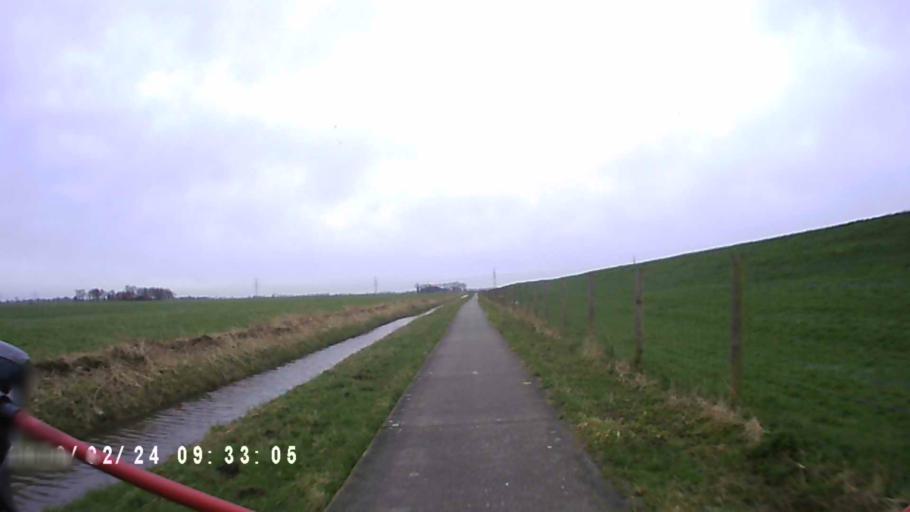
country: NL
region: Groningen
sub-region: Gemeente Winsum
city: Winsum
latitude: 53.3025
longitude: 6.4987
